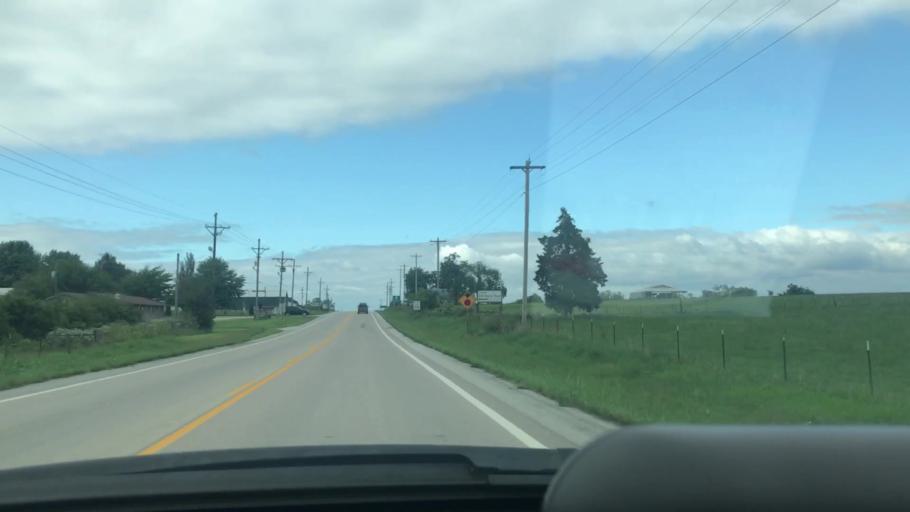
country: US
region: Missouri
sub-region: Hickory County
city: Hermitage
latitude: 37.9365
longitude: -93.2083
